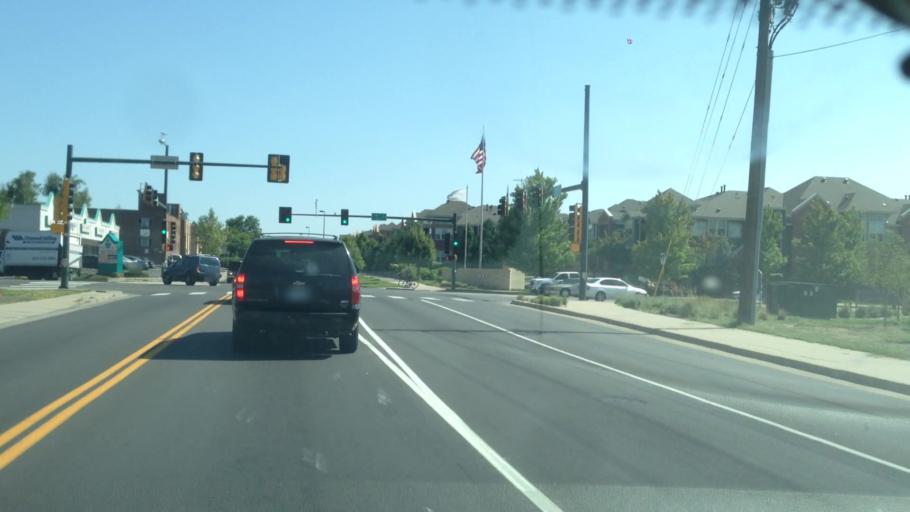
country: US
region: Colorado
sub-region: Adams County
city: Aurora
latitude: 39.7261
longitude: -104.8753
